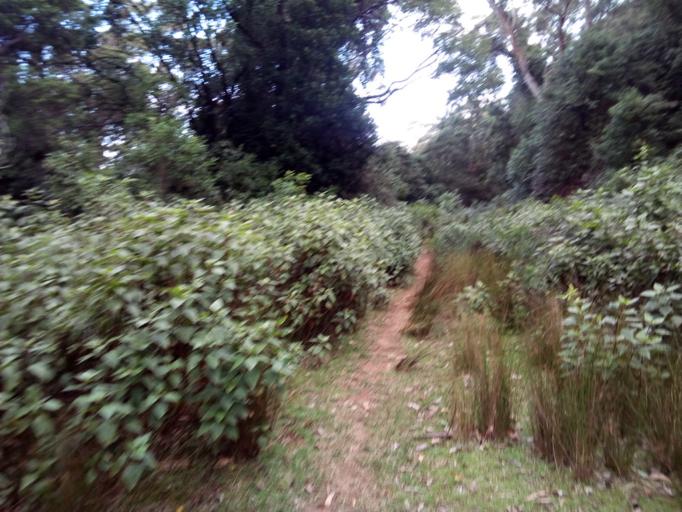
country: AU
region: New South Wales
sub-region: Wollongong
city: Mount Ousley
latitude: -34.4026
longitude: 150.8626
